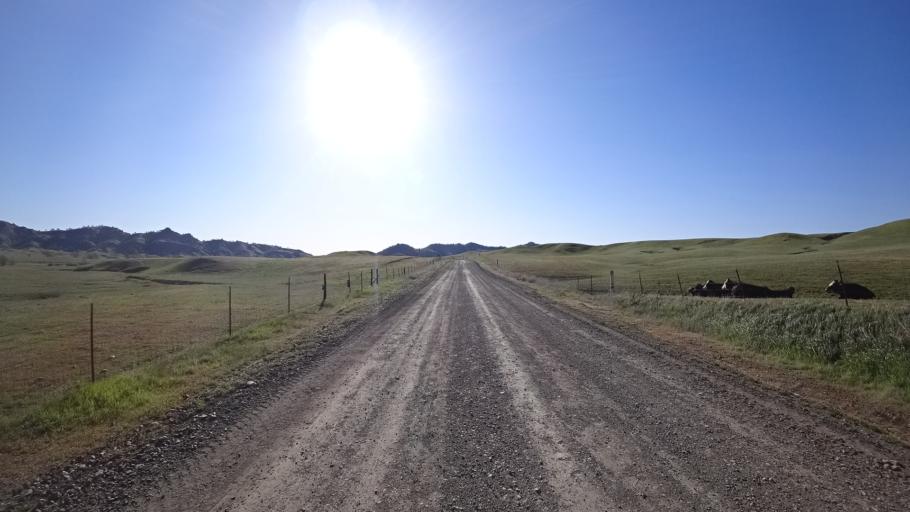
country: US
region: California
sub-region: Tehama County
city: Rancho Tehama Reserve
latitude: 39.7977
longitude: -122.5518
